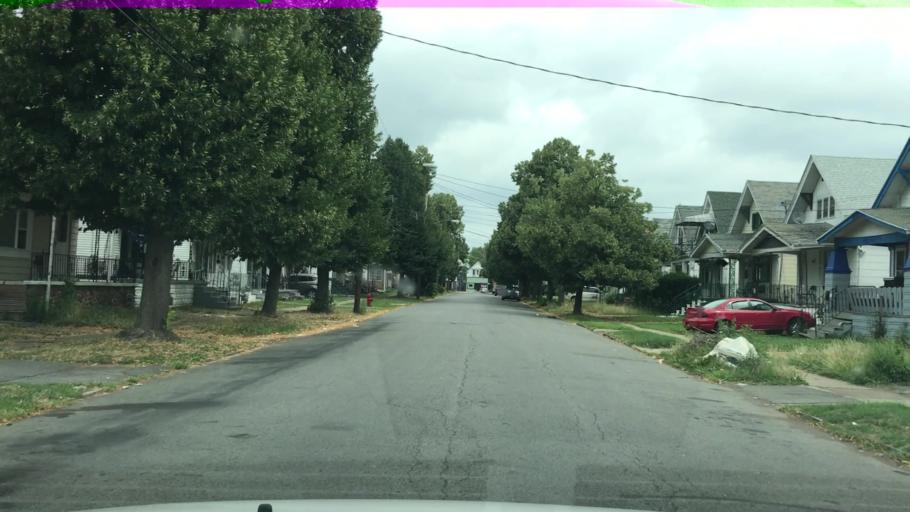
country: US
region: New York
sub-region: Erie County
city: Sloan
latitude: 42.9146
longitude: -78.8037
